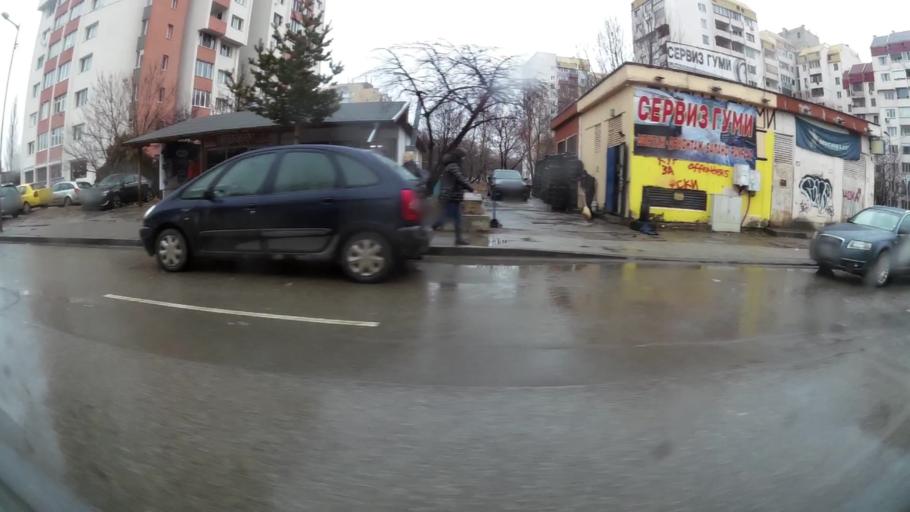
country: BG
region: Sofia-Capital
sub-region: Stolichna Obshtina
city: Sofia
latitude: 42.6411
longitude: 23.3831
